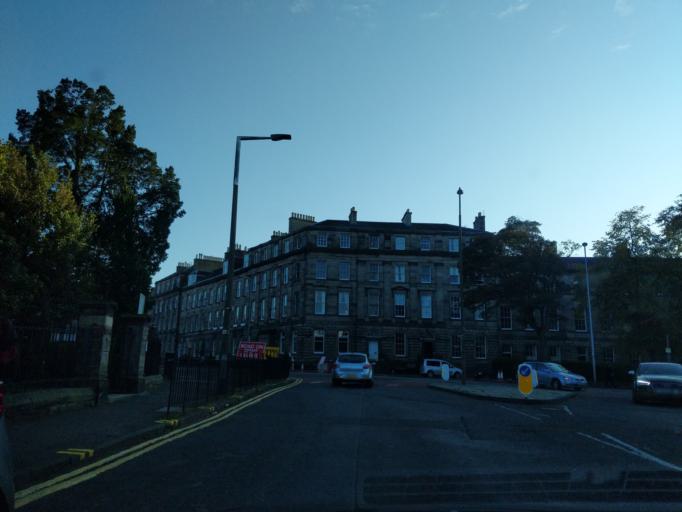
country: GB
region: Scotland
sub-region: Edinburgh
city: Edinburgh
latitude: 55.9604
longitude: -3.1915
